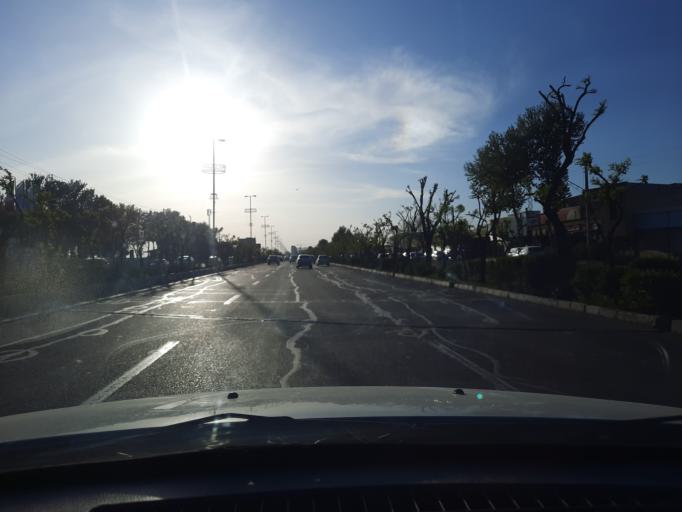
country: IR
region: Qazvin
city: Qazvin
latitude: 36.2627
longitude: 50.0418
